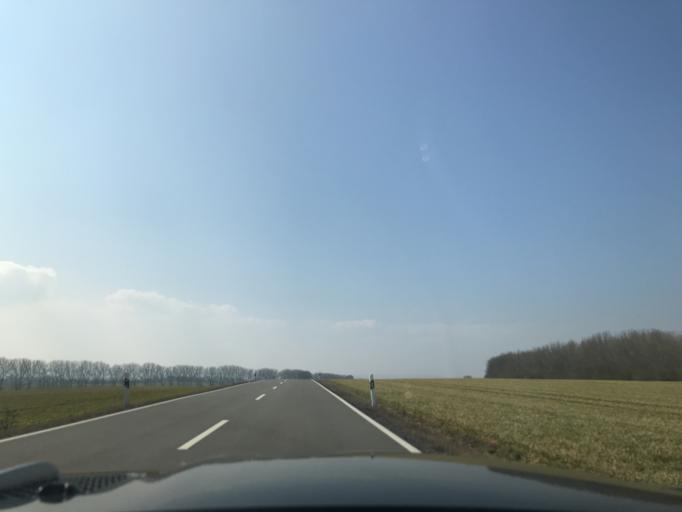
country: DE
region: Thuringia
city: Grossengottern
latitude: 51.1354
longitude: 10.6002
